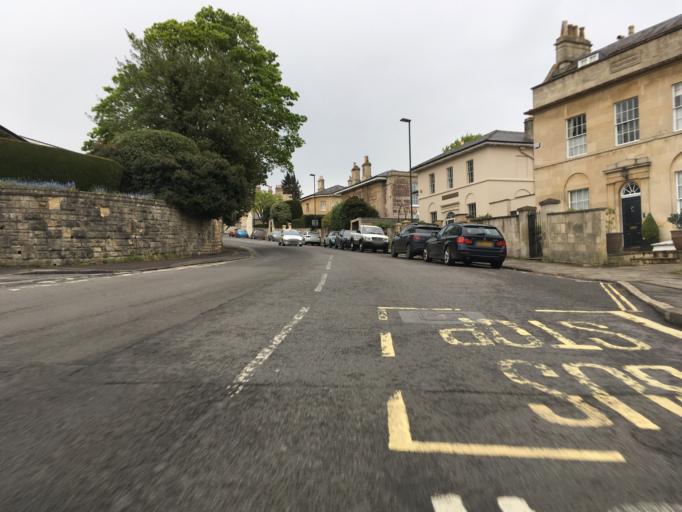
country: GB
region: England
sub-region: Bath and North East Somerset
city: Bath
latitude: 51.3809
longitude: -2.3456
